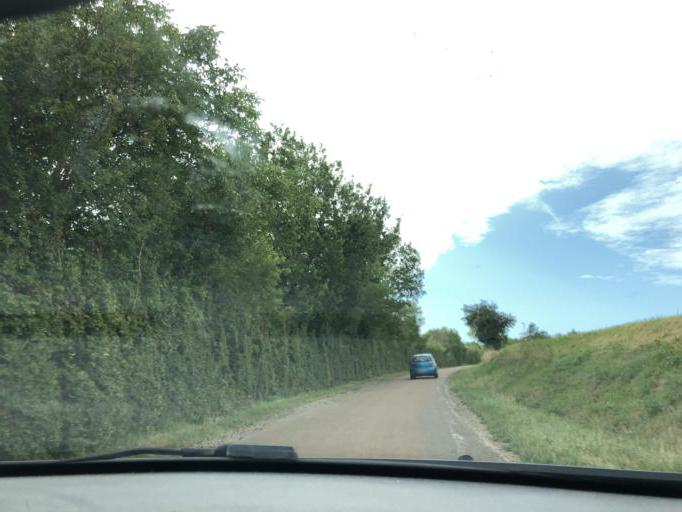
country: FR
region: Bourgogne
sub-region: Departement de l'Yonne
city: Chablis
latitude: 47.7861
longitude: 3.8336
